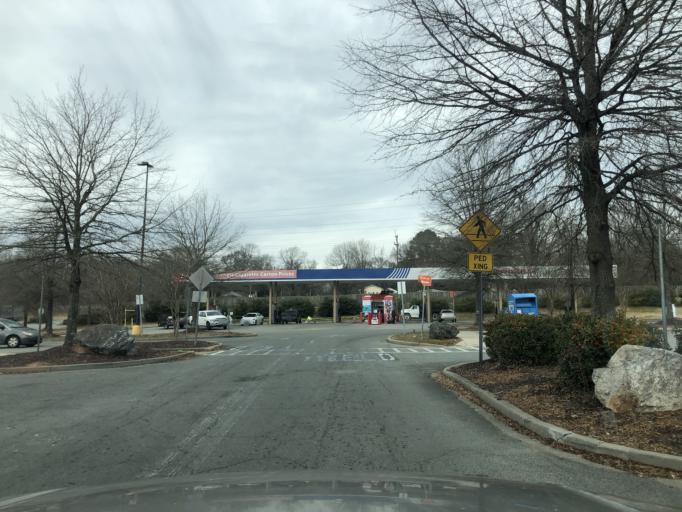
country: US
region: North Carolina
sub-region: Gaston County
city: Gastonia
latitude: 35.2612
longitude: -81.2239
